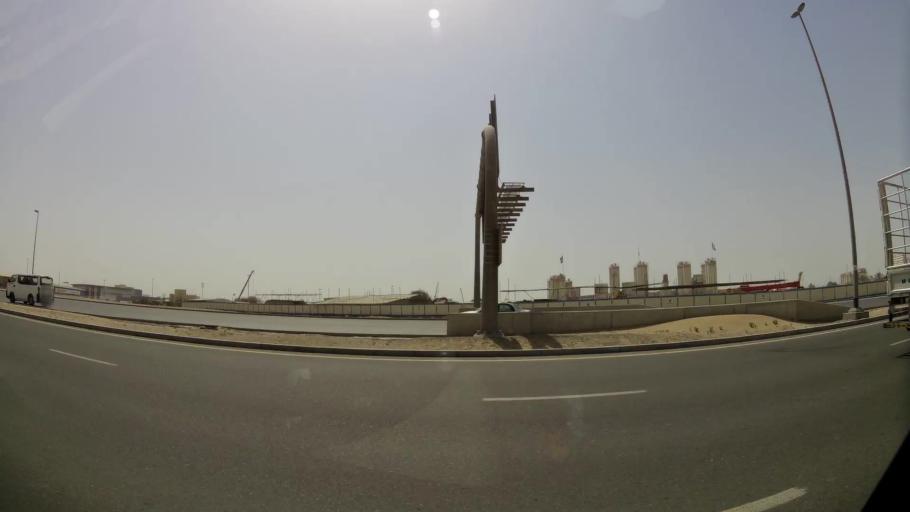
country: AE
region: Dubai
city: Dubai
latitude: 25.1569
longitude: 55.2367
